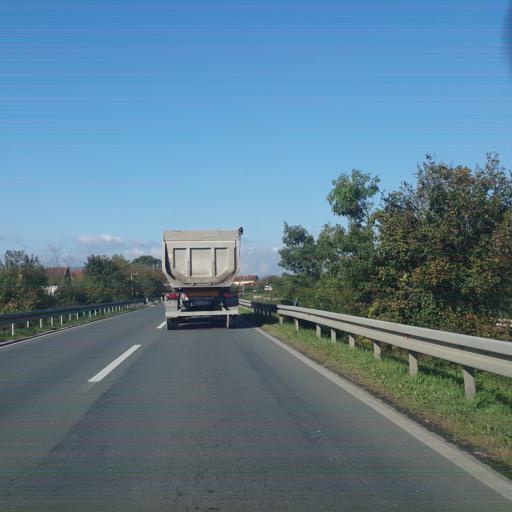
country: RS
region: Central Serbia
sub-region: Raski Okrug
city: Vrnjacka Banja
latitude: 43.6341
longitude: 20.9445
